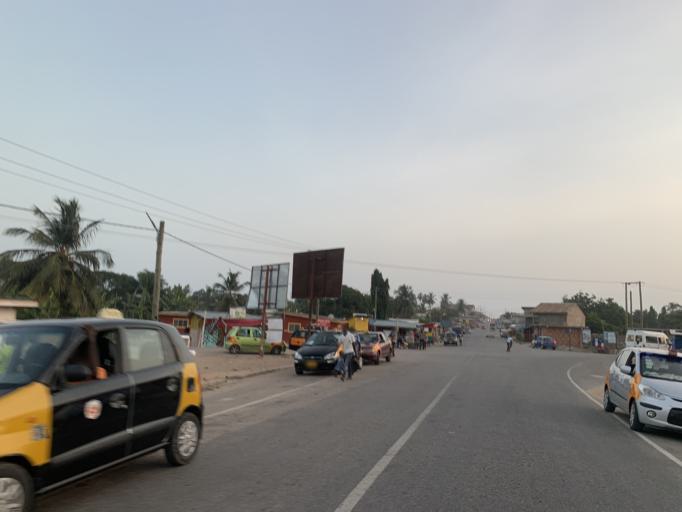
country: GH
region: Central
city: Winneba
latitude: 5.3570
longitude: -0.6104
